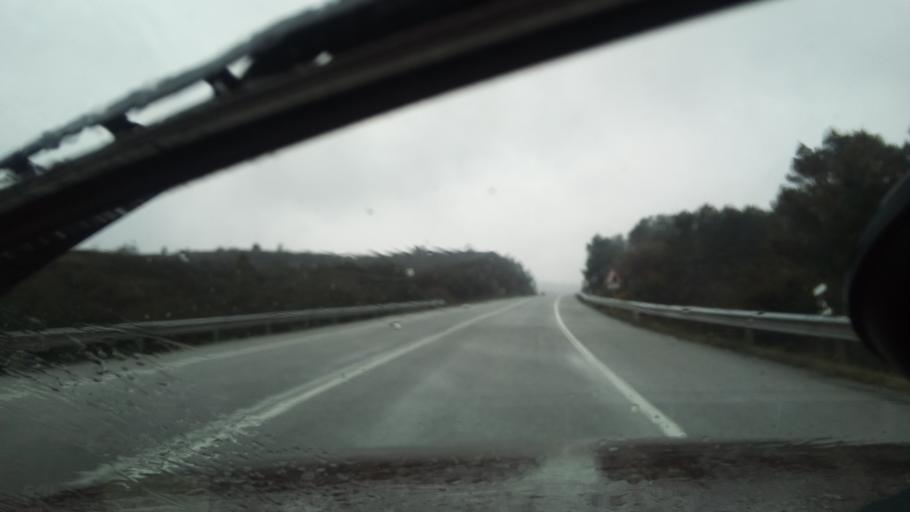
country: PT
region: Guarda
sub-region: Fornos de Algodres
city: Fornos de Algodres
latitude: 40.6032
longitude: -7.5815
